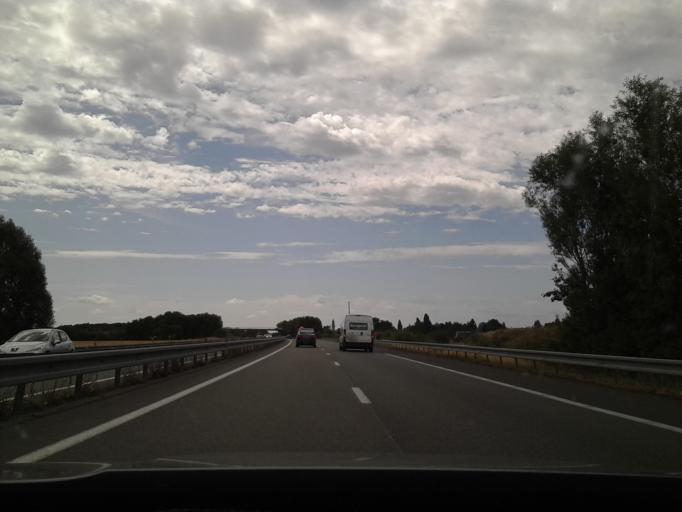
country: FR
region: Pays de la Loire
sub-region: Departement de la Sarthe
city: La Bazoge
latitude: 48.1208
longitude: 0.1466
